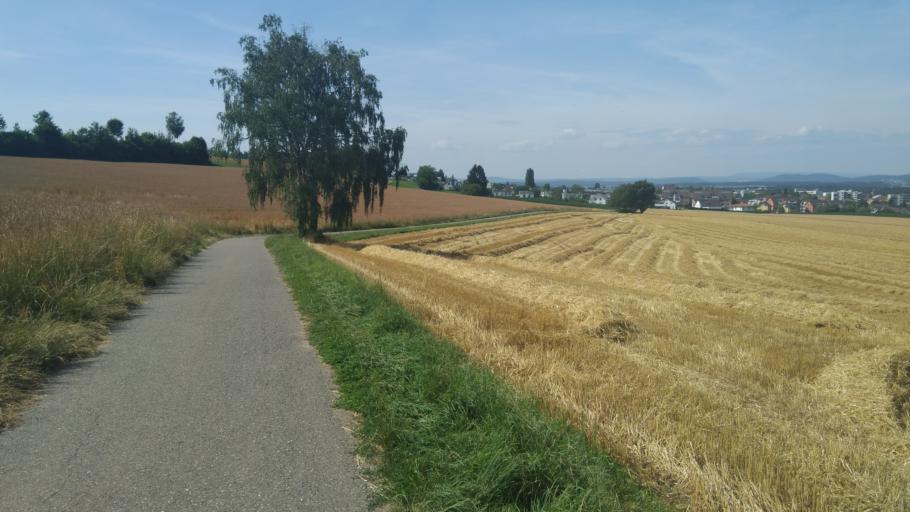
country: CH
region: Zurich
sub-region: Bezirk Dielsdorf
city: Ruemlang / Ruemlang (Dorfkern)
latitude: 47.4383
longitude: 8.5302
